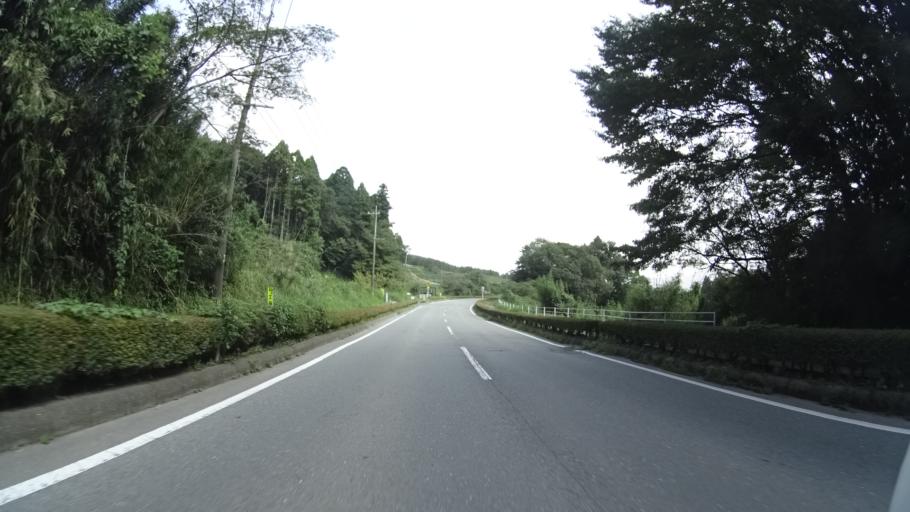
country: JP
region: Kumamoto
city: Aso
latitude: 32.8453
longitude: 131.0392
